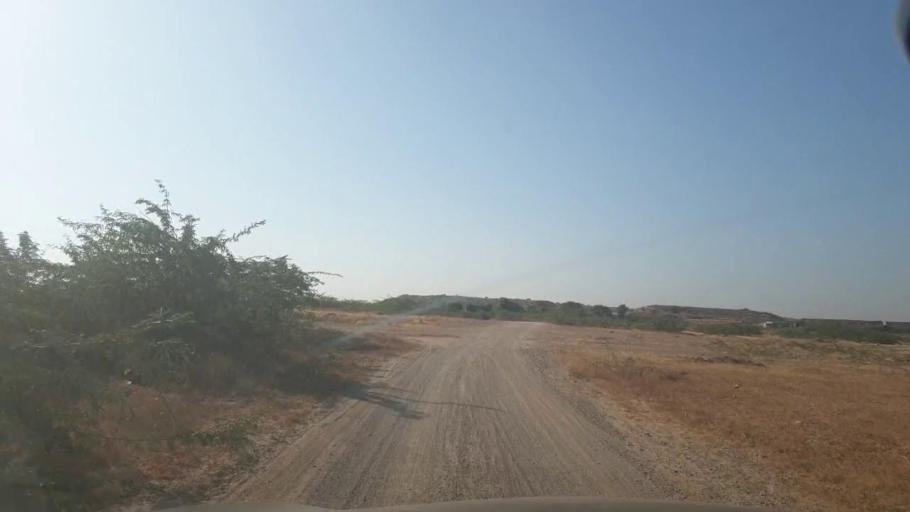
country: PK
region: Sindh
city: Malir Cantonment
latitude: 25.0376
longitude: 67.2608
